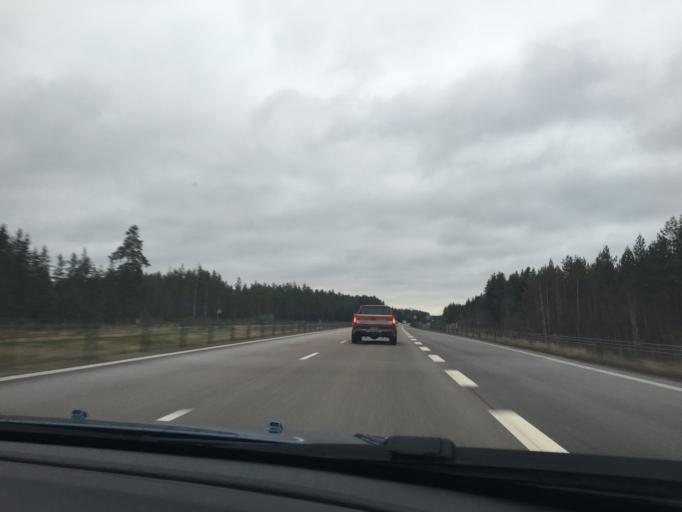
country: SE
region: Uppsala
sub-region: Alvkarleby Kommun
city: AElvkarleby
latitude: 60.4428
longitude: 17.4192
